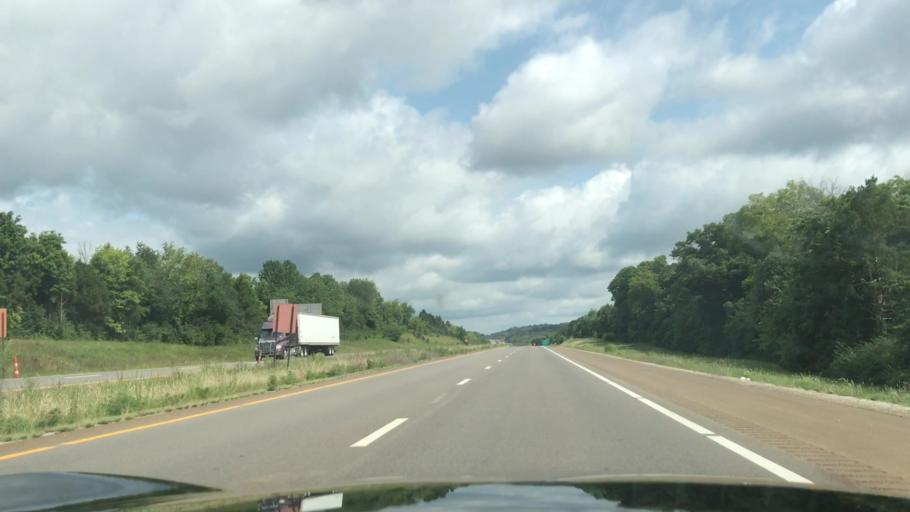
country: US
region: Kentucky
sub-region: Warren County
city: Bowling Green
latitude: 36.9801
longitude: -86.5012
